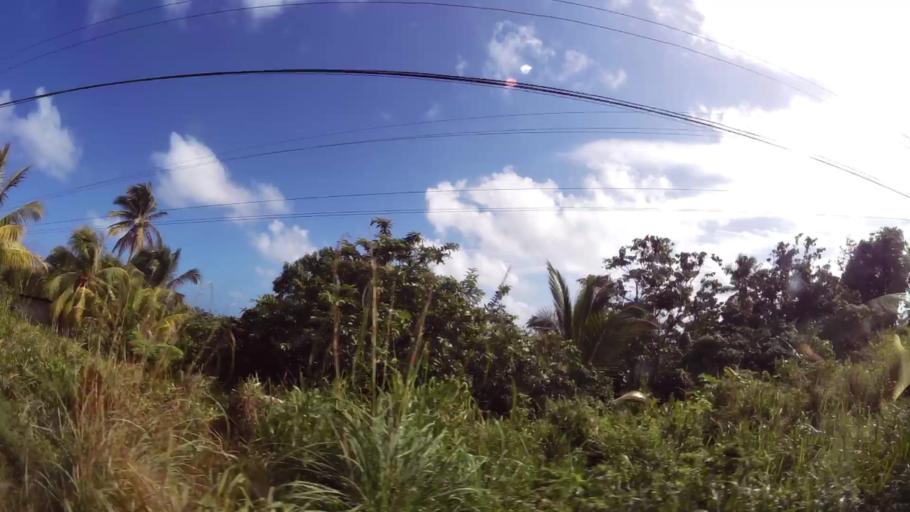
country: DM
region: Saint David
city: Castle Bruce
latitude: 15.4702
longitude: -61.2490
